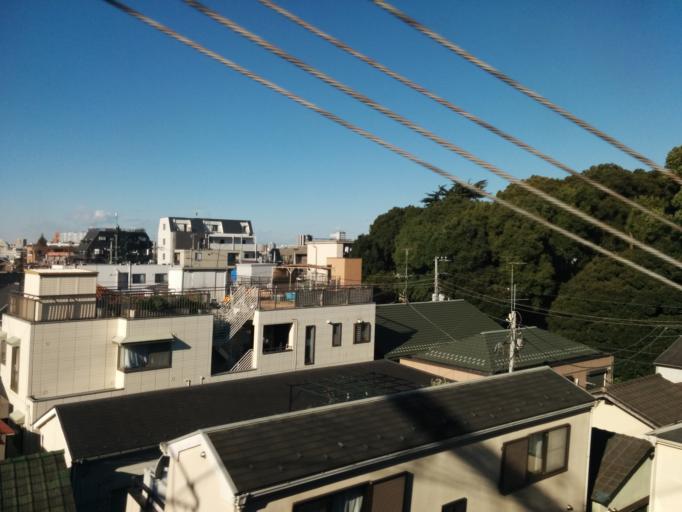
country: JP
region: Kanagawa
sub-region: Kawasaki-shi
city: Kawasaki
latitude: 35.5998
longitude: 139.7208
